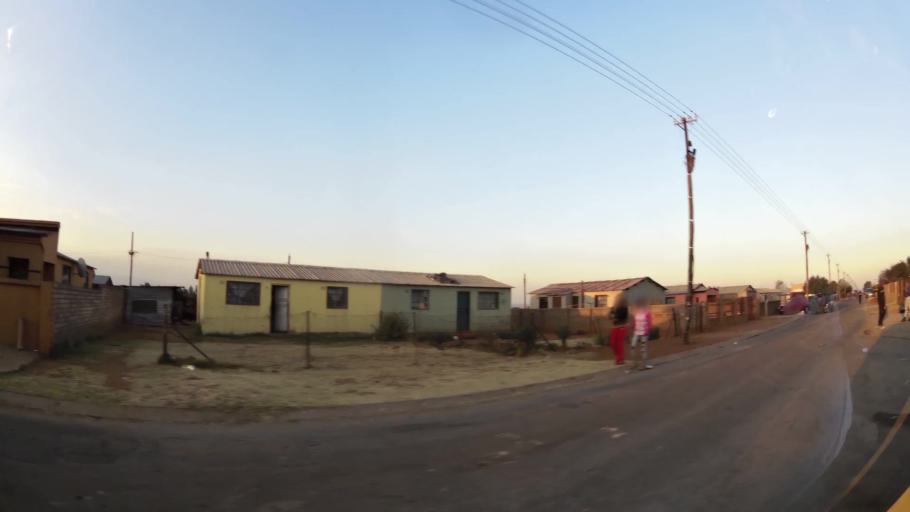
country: ZA
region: Gauteng
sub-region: West Rand District Municipality
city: Randfontein
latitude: -26.2008
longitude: 27.7118
